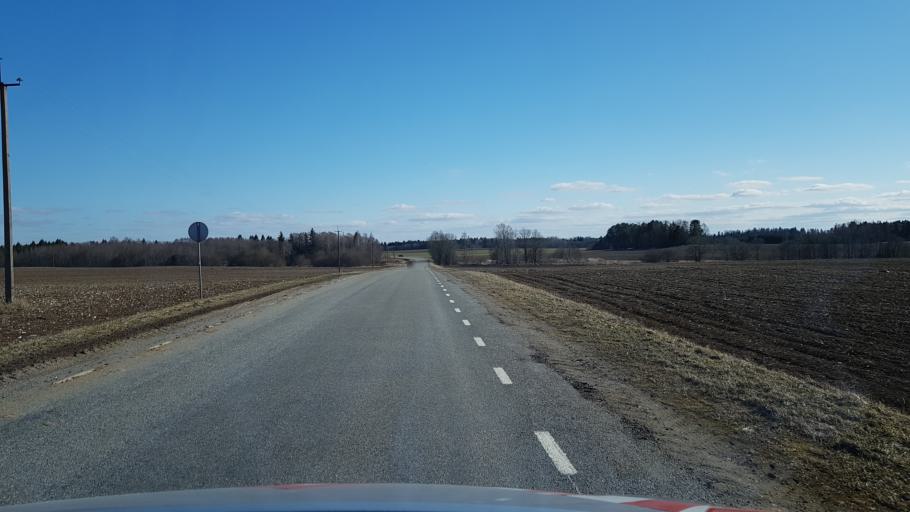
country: EE
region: Laeaene-Virumaa
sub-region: Kadrina vald
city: Kadrina
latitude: 59.3709
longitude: 26.0463
